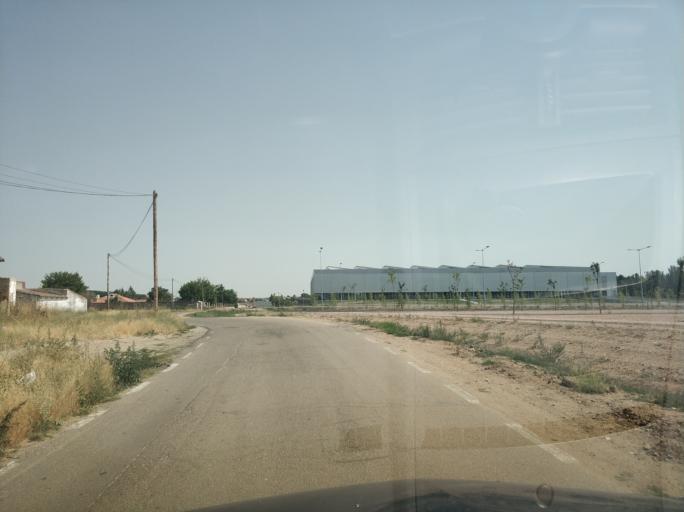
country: ES
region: Castille and Leon
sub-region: Provincia de Salamanca
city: Santa Marta de Tormes
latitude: 40.9635
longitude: -5.6365
